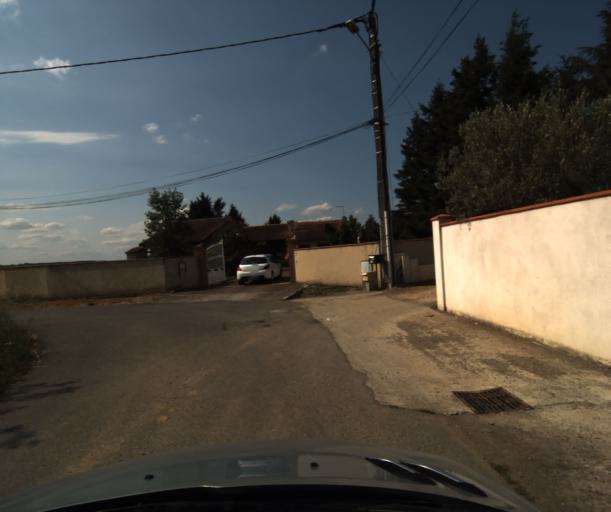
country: FR
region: Midi-Pyrenees
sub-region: Departement de la Haute-Garonne
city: Saint-Lys
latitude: 43.5204
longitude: 1.1864
